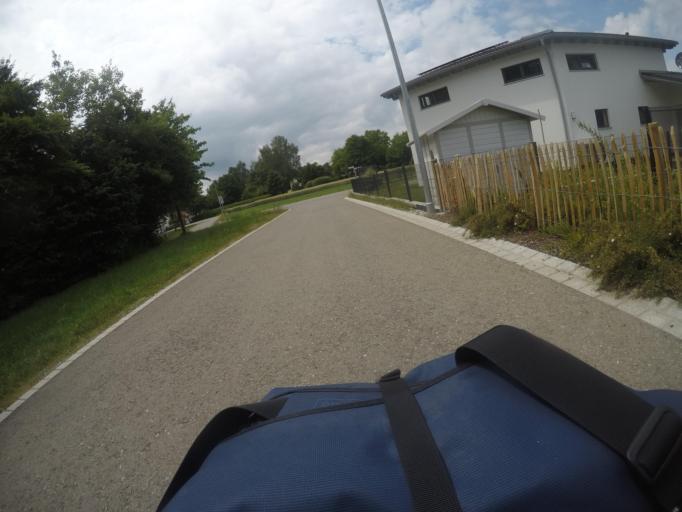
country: DE
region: Bavaria
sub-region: Swabia
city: Heimertingen
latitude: 48.0432
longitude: 10.1588
